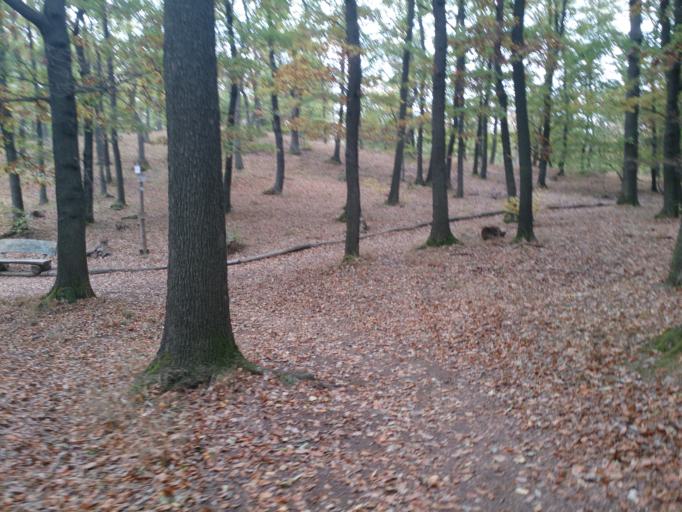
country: DE
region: Saxony-Anhalt
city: Wernigerode
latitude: 51.8237
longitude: 10.7802
